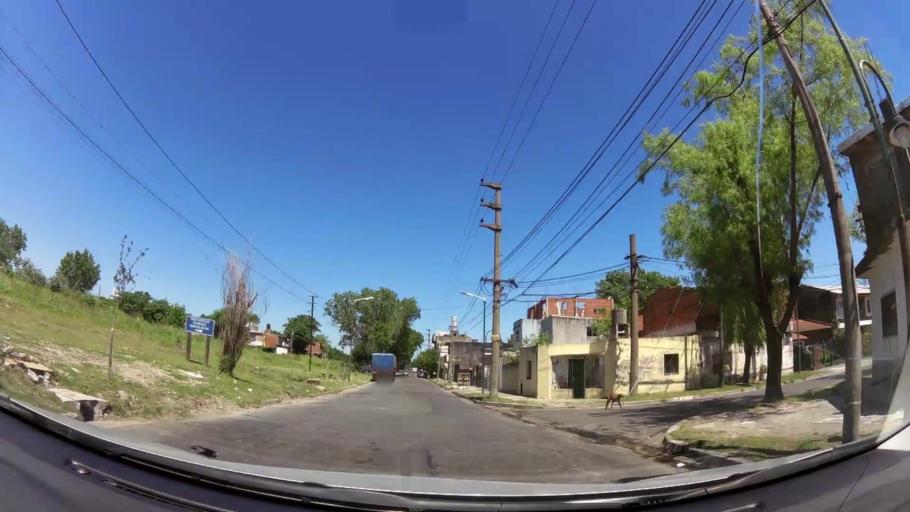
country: AR
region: Buenos Aires
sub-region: Partido de Tigre
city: Tigre
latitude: -34.4620
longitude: -58.5541
